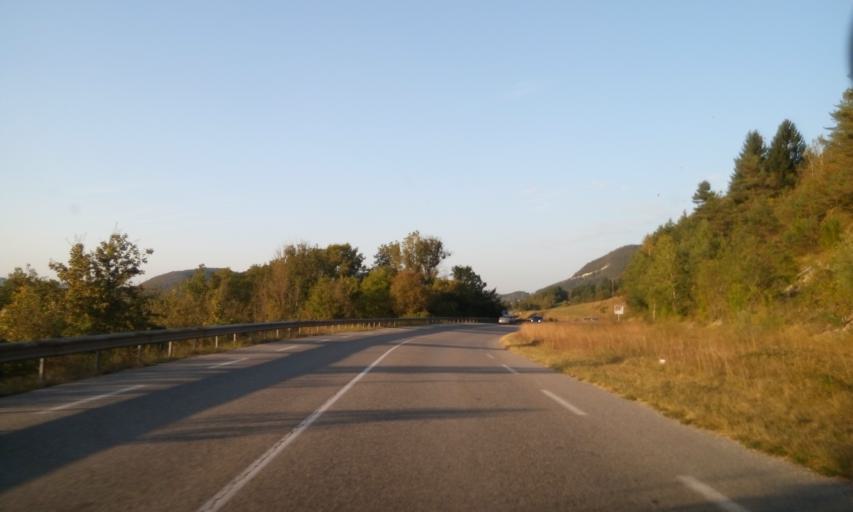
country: FR
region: Rhone-Alpes
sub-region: Departement de l'Ain
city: Saint-Martin-du-Frene
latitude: 46.1463
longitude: 5.5582
